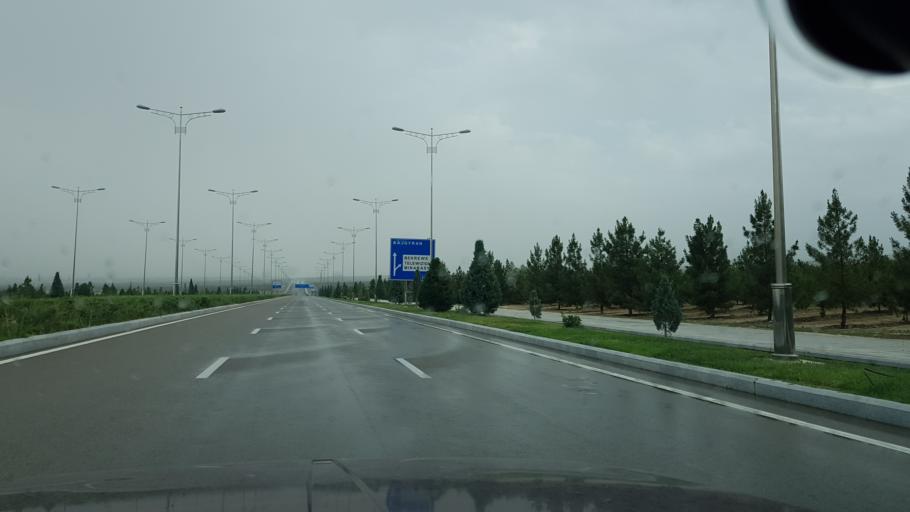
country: TM
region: Ahal
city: Ashgabat
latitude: 37.8820
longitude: 58.2734
